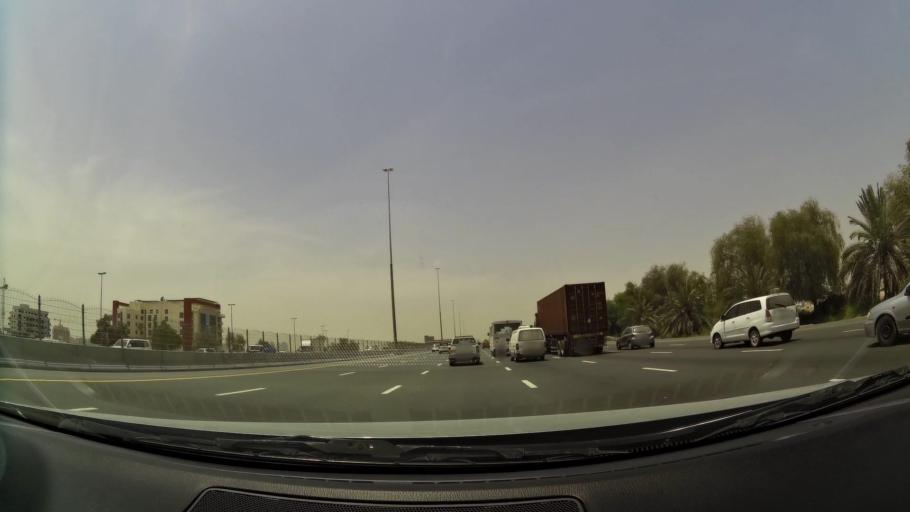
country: AE
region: Ash Shariqah
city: Sharjah
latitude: 25.1511
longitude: 55.3872
